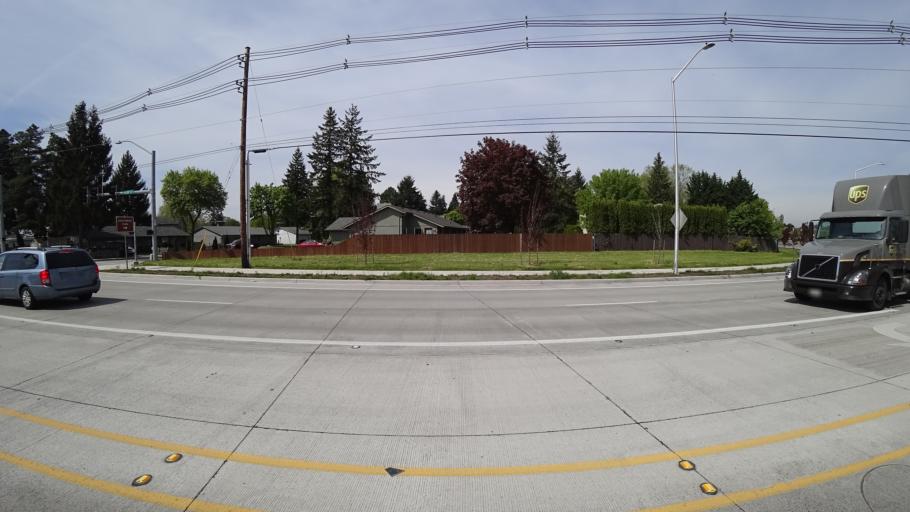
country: US
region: Oregon
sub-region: Washington County
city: Hillsboro
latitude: 45.5283
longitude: -122.9540
